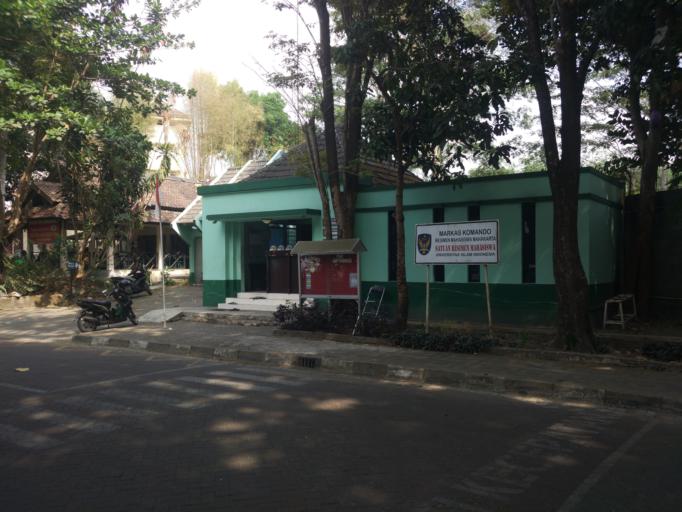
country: ID
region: Daerah Istimewa Yogyakarta
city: Sleman
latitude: -7.6865
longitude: 110.4154
